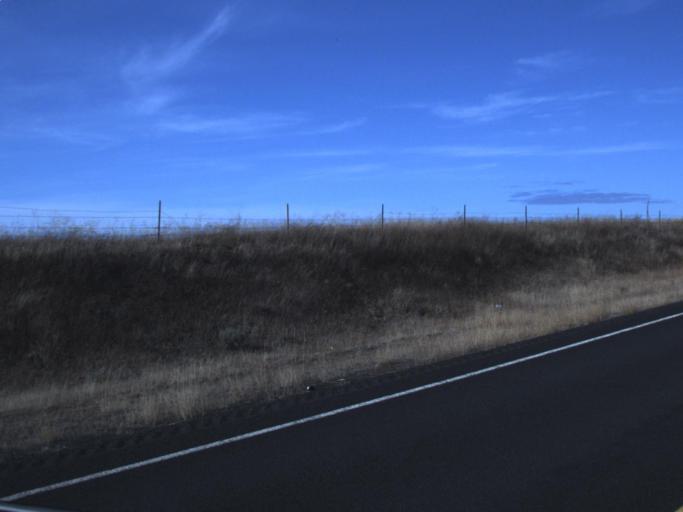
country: US
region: Washington
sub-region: Lincoln County
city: Davenport
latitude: 47.7496
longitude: -118.1724
